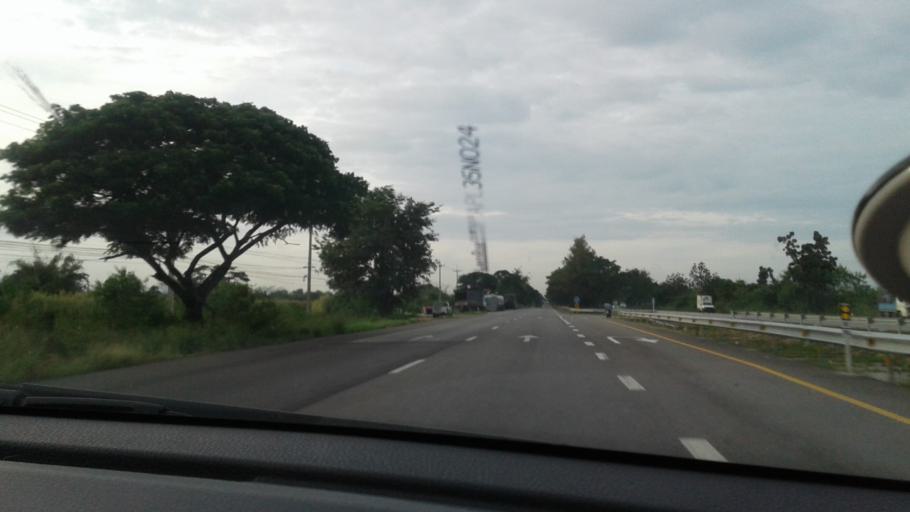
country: TH
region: Prachuap Khiri Khan
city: Pran Buri
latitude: 12.4470
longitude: 99.9060
